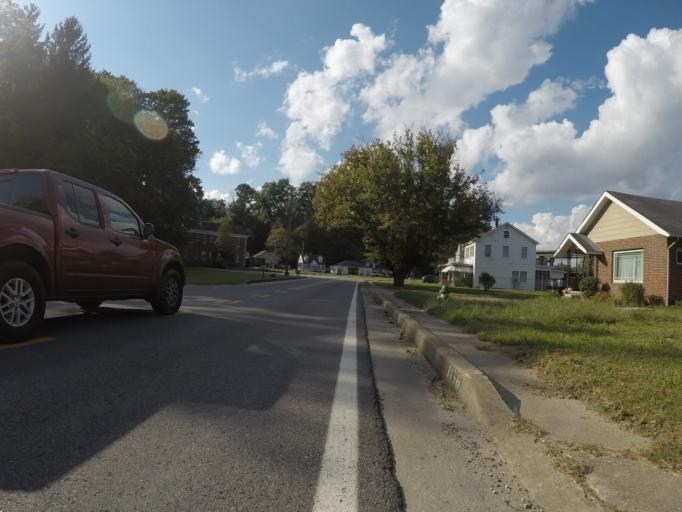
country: US
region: Ohio
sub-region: Lawrence County
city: Burlington
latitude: 38.3932
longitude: -82.5147
